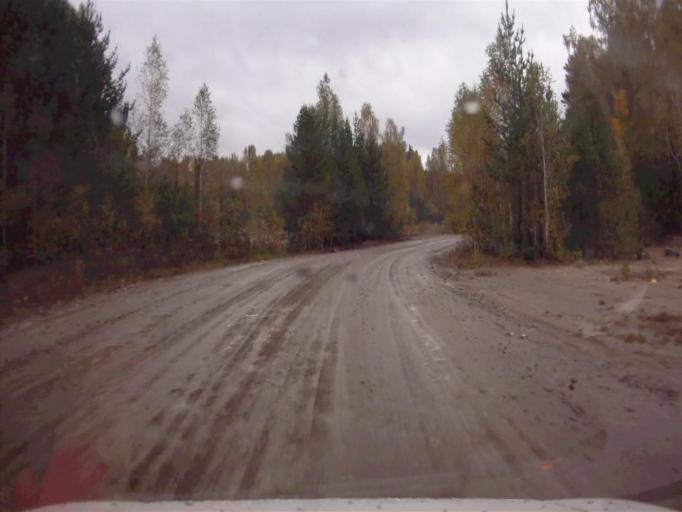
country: RU
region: Chelyabinsk
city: Kyshtym
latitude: 55.8247
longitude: 60.4847
